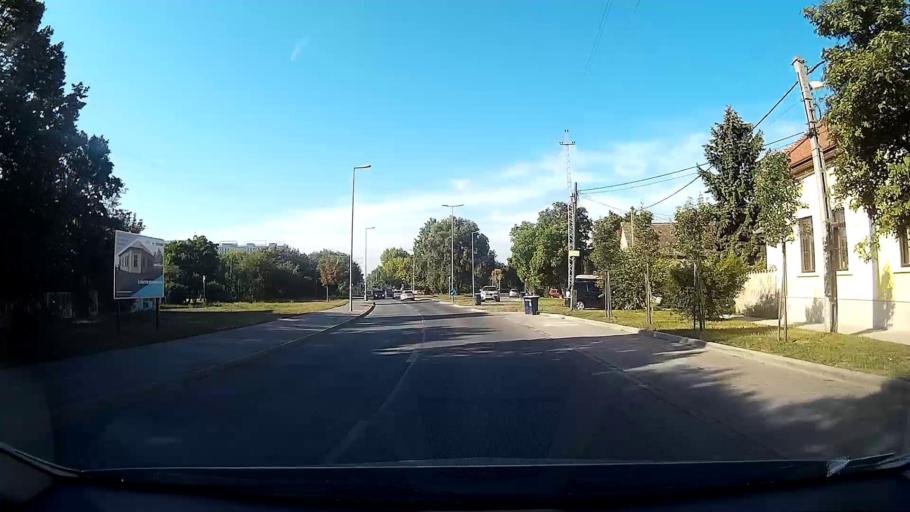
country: HU
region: Pest
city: Budakalasz
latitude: 47.5991
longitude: 19.0458
